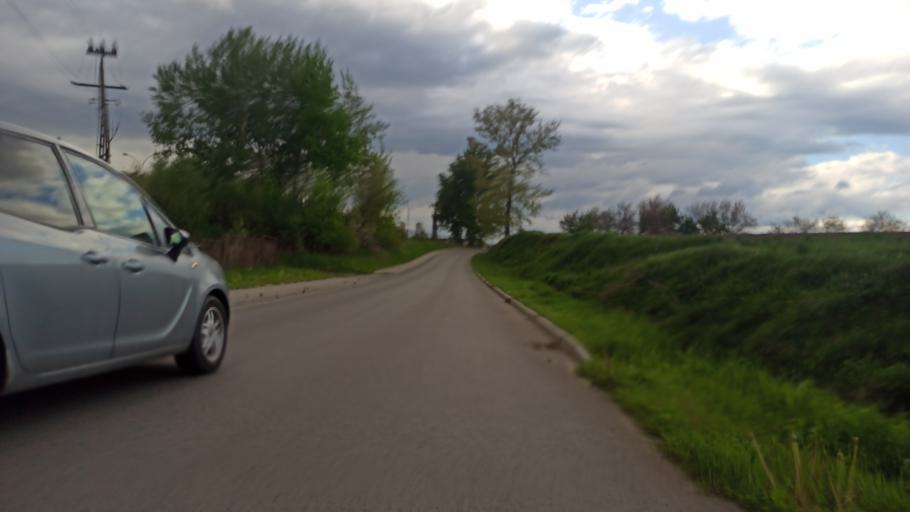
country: PL
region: Subcarpathian Voivodeship
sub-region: Powiat jaroslawski
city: Radymno
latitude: 49.9321
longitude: 22.8409
